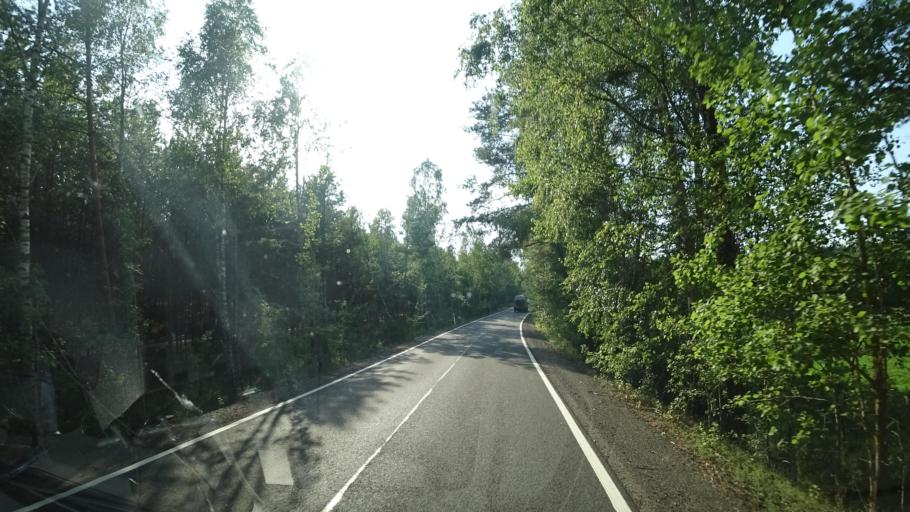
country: PL
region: Pomeranian Voivodeship
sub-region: Powiat chojnicki
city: Chojnice
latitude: 53.8550
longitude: 17.5572
